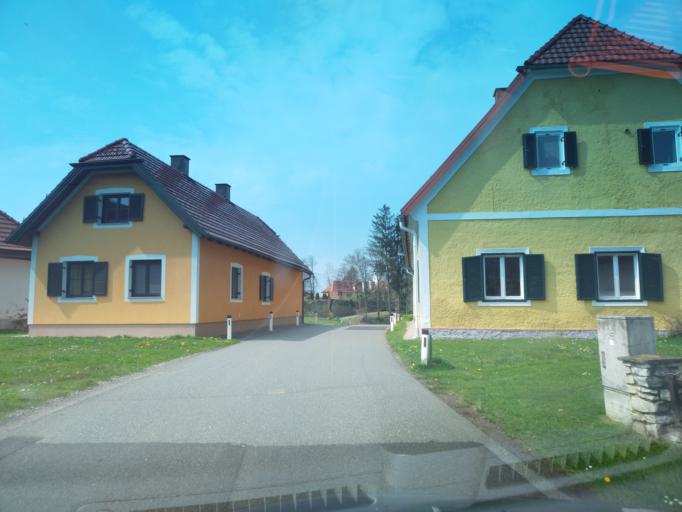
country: AT
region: Styria
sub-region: Politischer Bezirk Leibnitz
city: Kitzeck im Sausal
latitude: 46.7568
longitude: 15.4098
